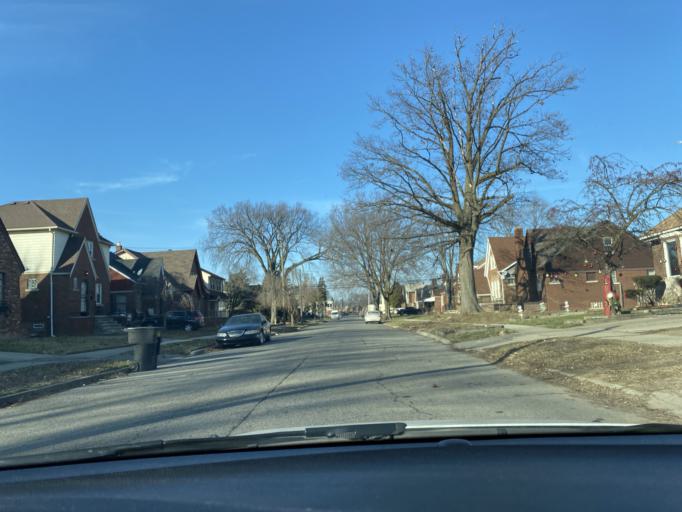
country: US
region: Michigan
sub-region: Wayne County
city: Harper Woods
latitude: 42.4079
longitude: -82.9448
